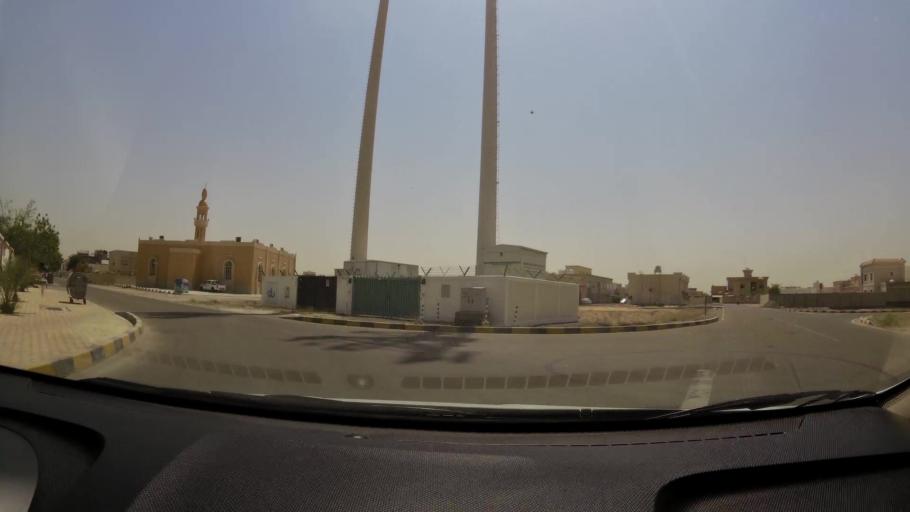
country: AE
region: Ajman
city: Ajman
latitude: 25.4227
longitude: 55.5250
